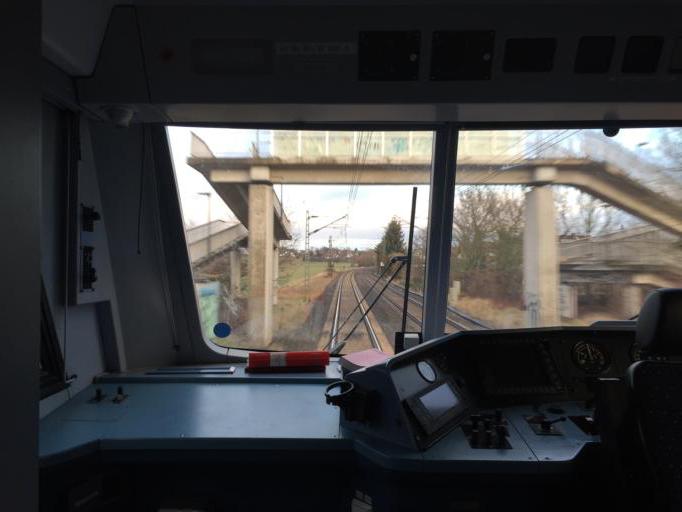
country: DE
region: Hesse
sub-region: Regierungsbezirk Darmstadt
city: Karben
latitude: 50.2463
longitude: 8.7518
